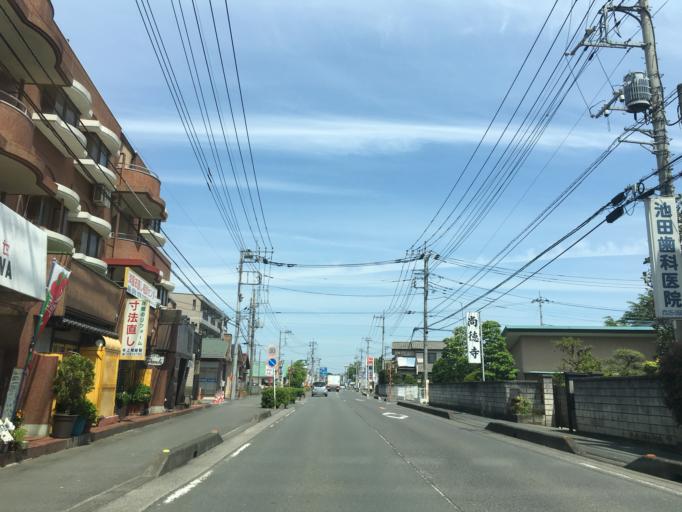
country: JP
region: Saitama
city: Okegawa
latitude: 35.9574
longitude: 139.5647
